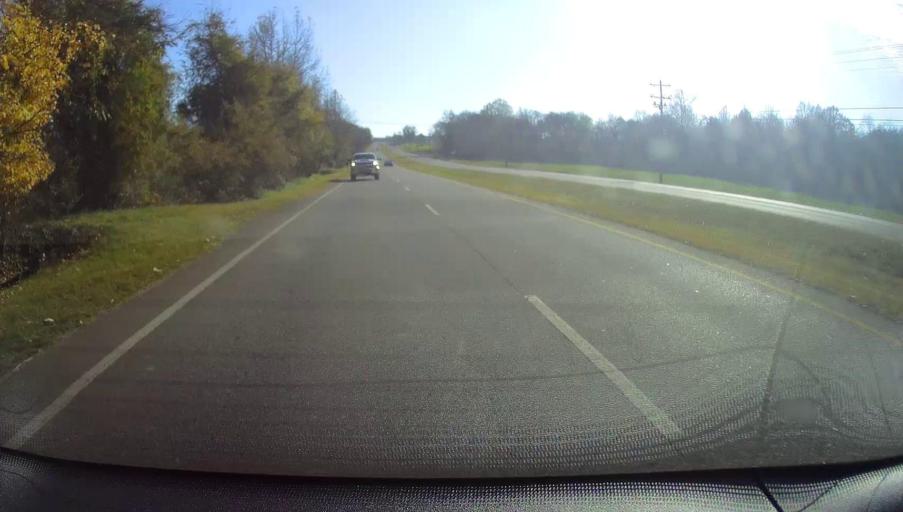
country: US
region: Alabama
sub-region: Limestone County
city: Athens
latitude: 34.7410
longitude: -86.9570
